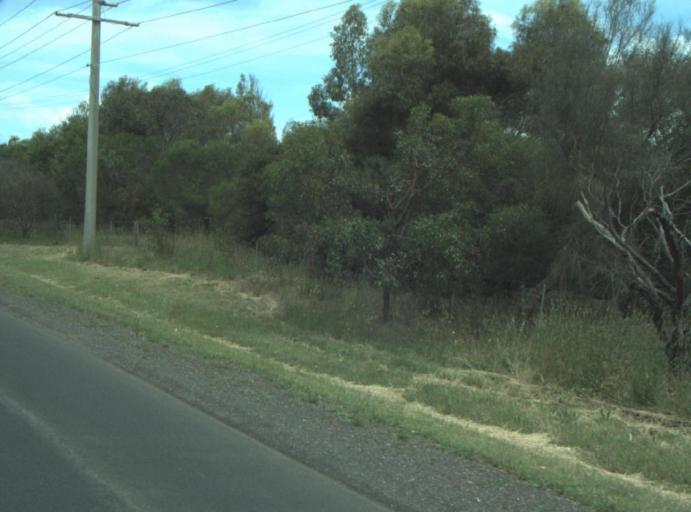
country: AU
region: Victoria
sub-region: Greater Geelong
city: Wandana Heights
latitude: -38.2283
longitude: 144.2987
